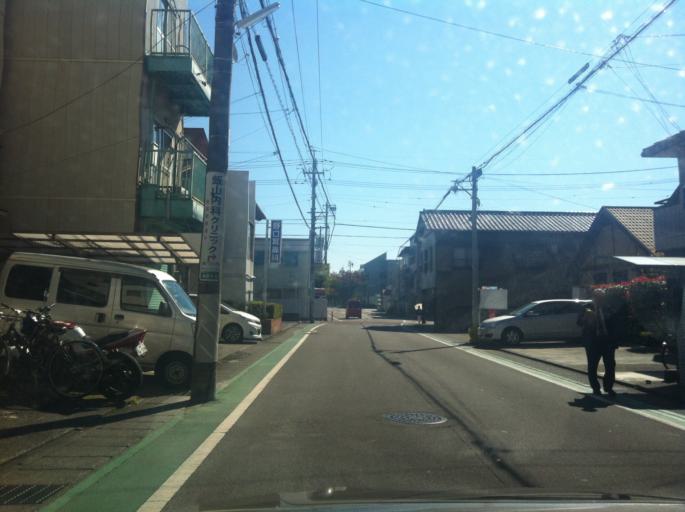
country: JP
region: Shizuoka
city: Shizuoka-shi
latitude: 34.9745
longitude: 138.4044
